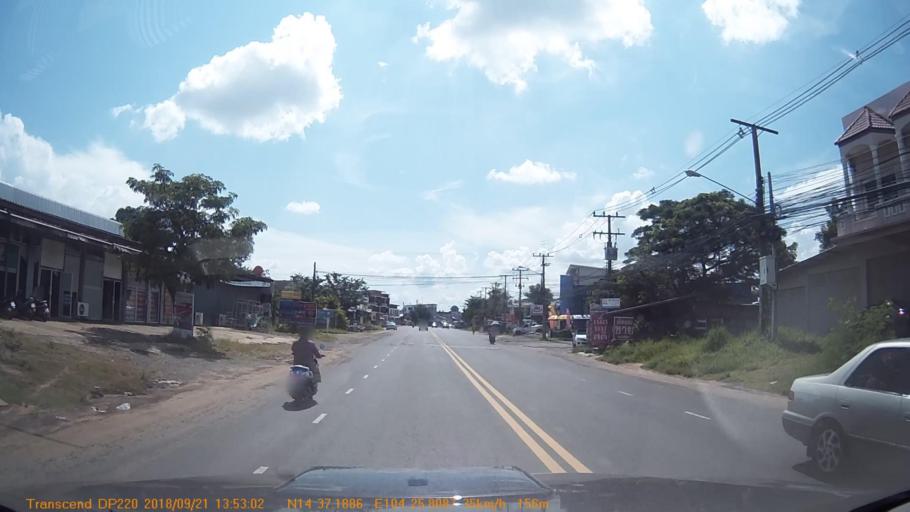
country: TH
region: Sisaket
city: Khun Han
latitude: 14.6197
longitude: 104.4300
